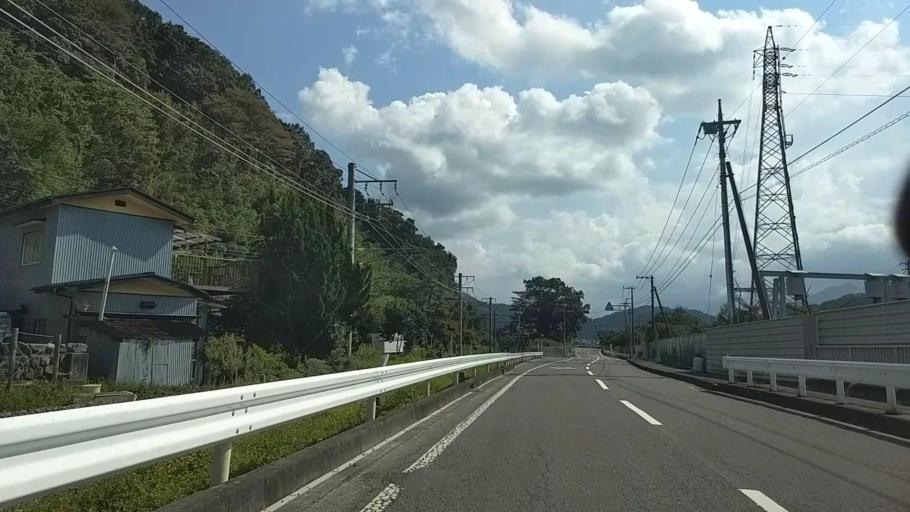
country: JP
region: Shizuoka
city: Fujinomiya
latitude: 35.3764
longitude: 138.4522
